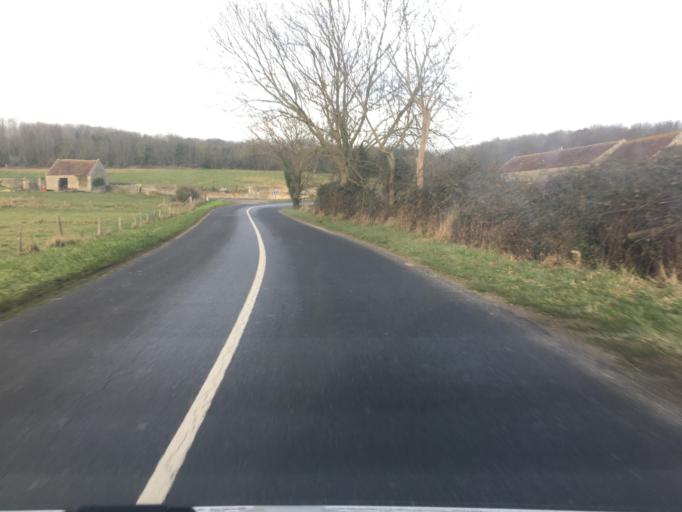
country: FR
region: Lower Normandy
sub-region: Departement du Calvados
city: Creully
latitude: 49.2885
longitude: -0.5415
